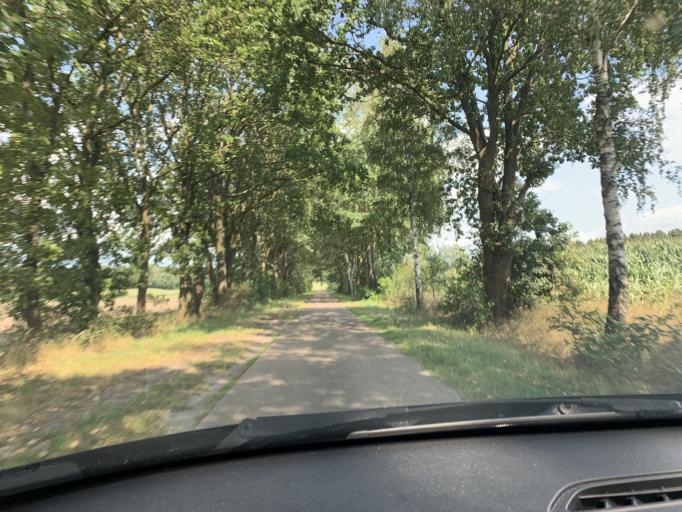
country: DE
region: Lower Saxony
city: Undeloh
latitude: 53.2234
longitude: 9.9123
